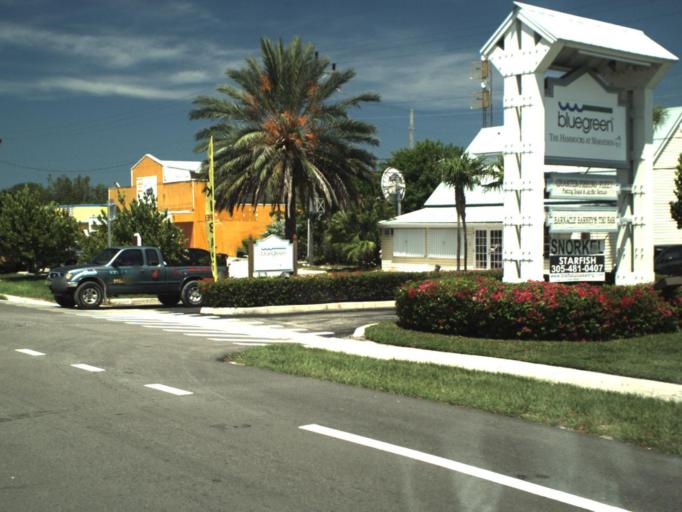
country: US
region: Florida
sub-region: Monroe County
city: Marathon
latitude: 24.7086
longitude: -81.1072
